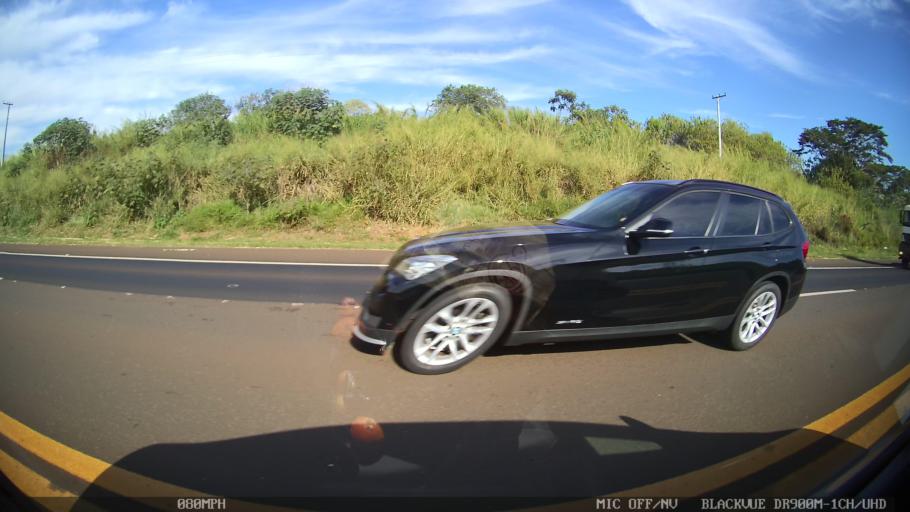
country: BR
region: Sao Paulo
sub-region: Araraquara
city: Araraquara
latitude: -21.7881
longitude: -48.1229
